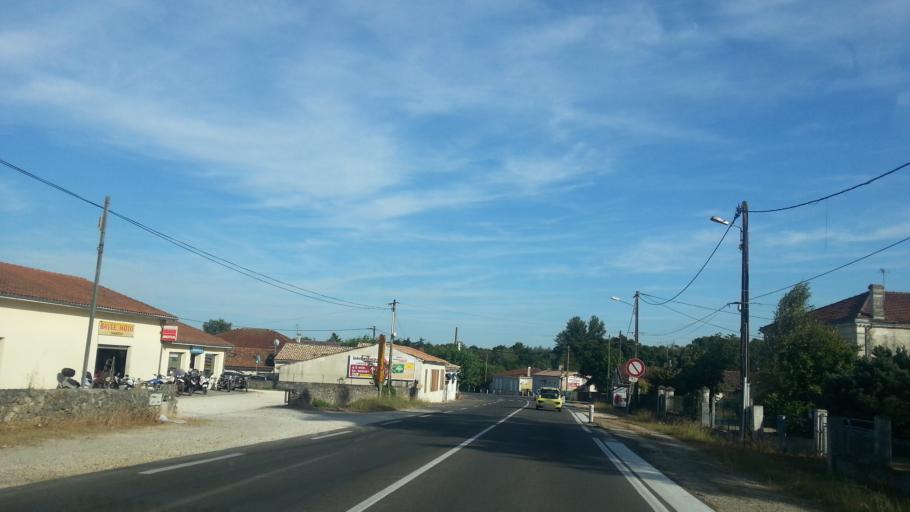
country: FR
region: Aquitaine
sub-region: Departement de la Gironde
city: Paillet
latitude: 44.6624
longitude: -0.3829
